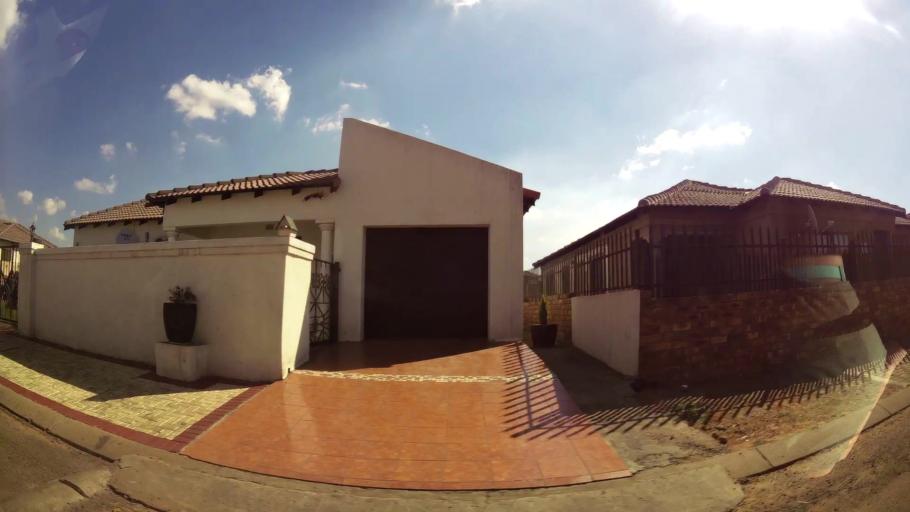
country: ZA
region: Mpumalanga
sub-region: Nkangala District Municipality
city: Witbank
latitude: -25.9497
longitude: 29.2496
